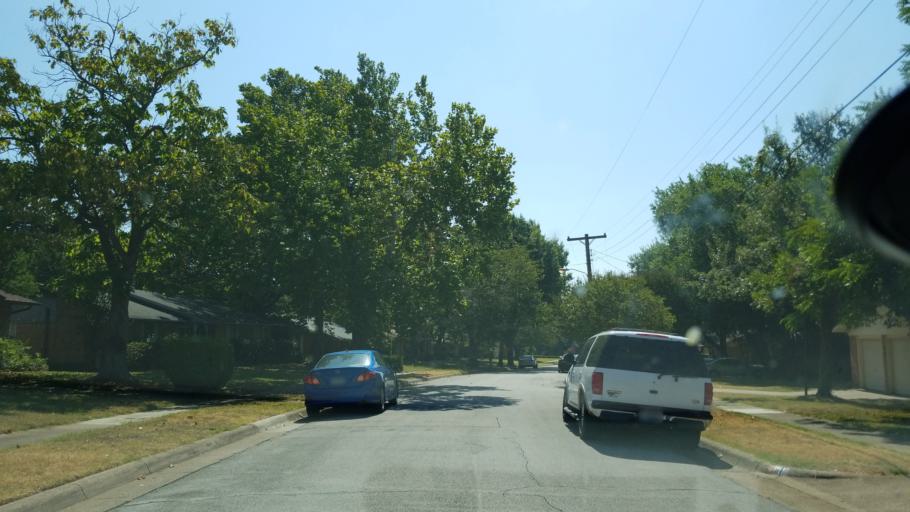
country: US
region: Texas
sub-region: Dallas County
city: Duncanville
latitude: 32.6554
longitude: -96.9044
